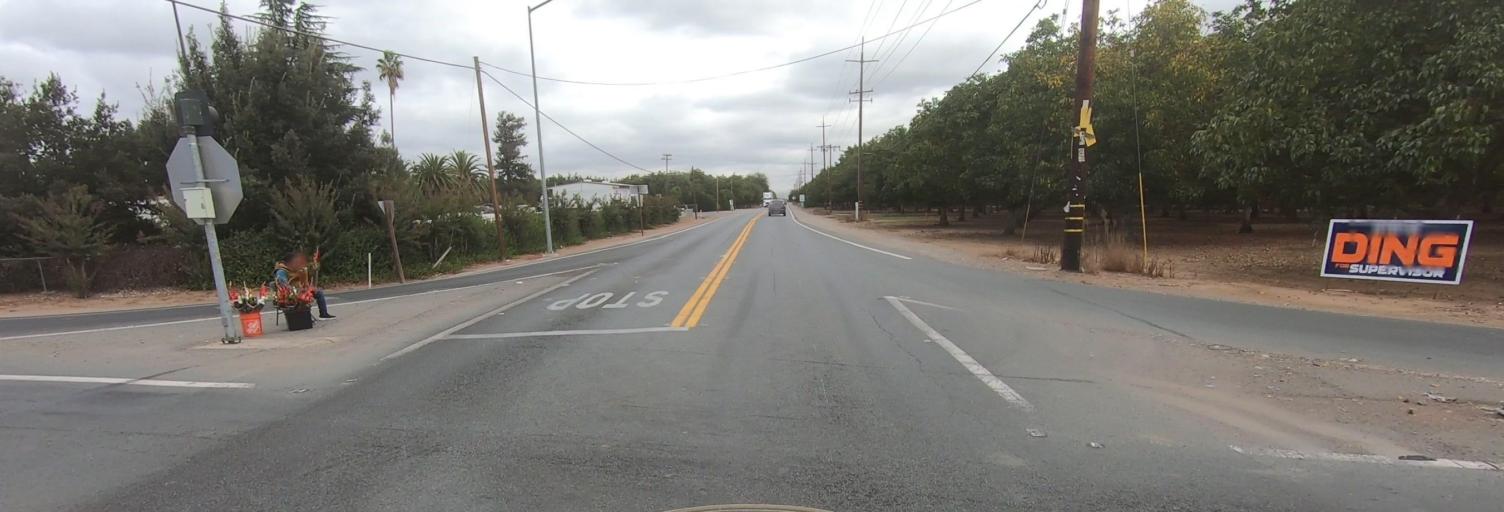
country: US
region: California
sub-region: San Joaquin County
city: Linden
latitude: 38.0007
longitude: -121.1496
